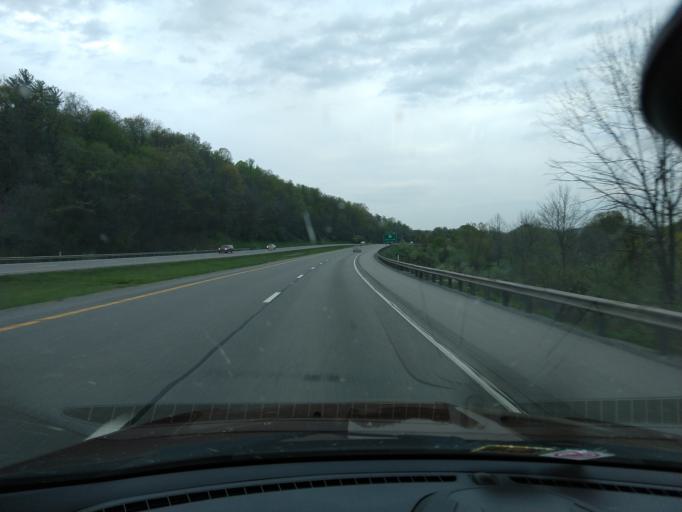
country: US
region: West Virginia
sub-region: Lewis County
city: Weston
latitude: 39.0726
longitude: -80.4052
